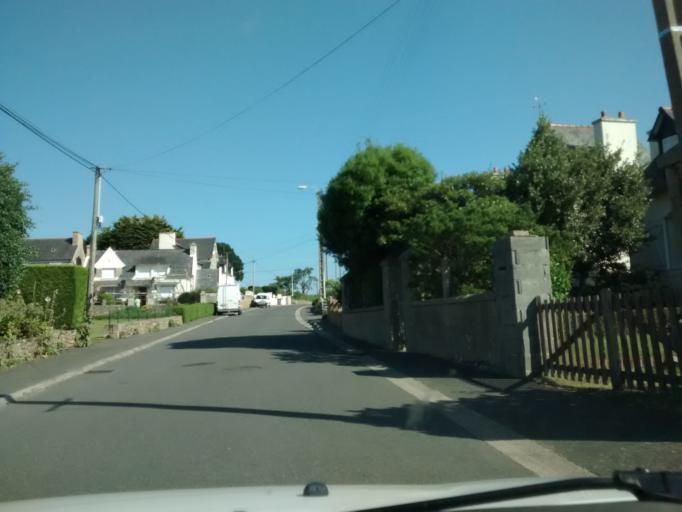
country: FR
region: Brittany
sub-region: Departement des Cotes-d'Armor
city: Pleubian
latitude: 48.8615
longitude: -3.1037
